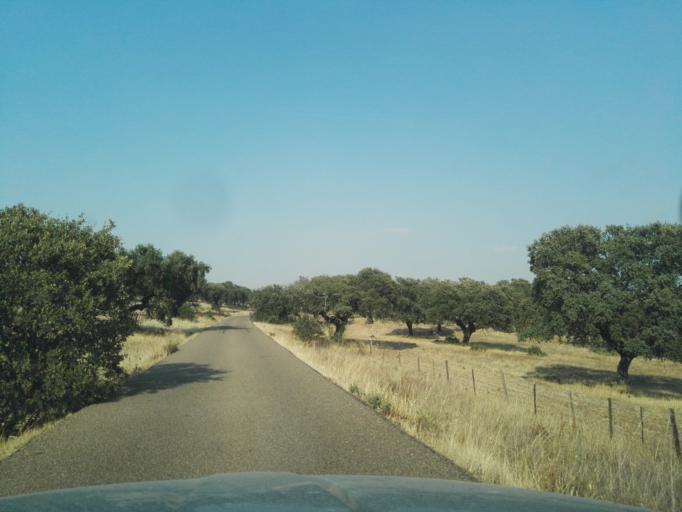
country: PT
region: Portalegre
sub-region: Campo Maior
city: Campo Maior
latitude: 38.9926
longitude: -7.1661
